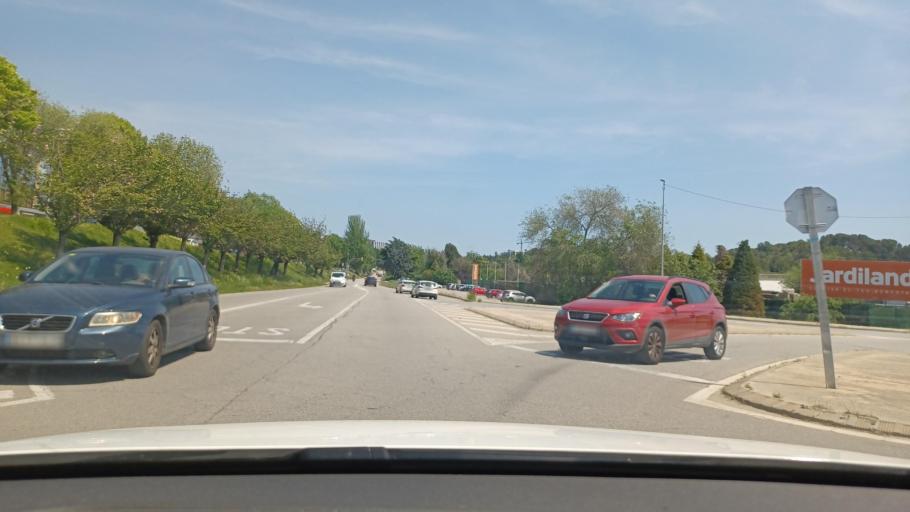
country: ES
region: Catalonia
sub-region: Provincia de Barcelona
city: Rubi
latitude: 41.4801
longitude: 2.0569
